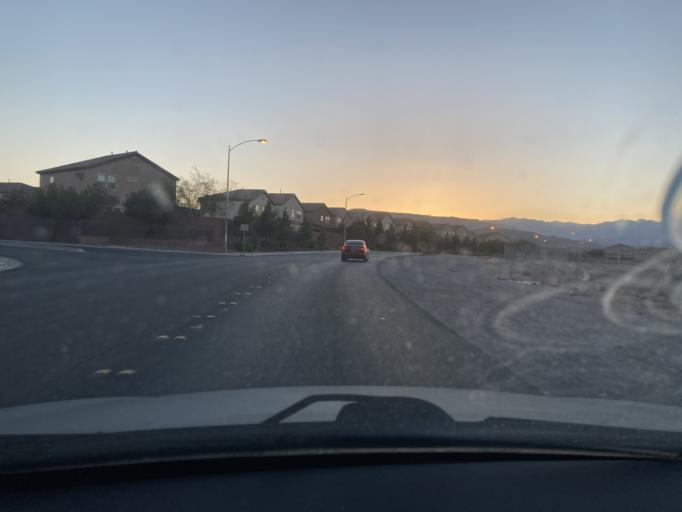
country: US
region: Nevada
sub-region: Clark County
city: Enterprise
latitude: 36.0611
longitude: -115.2842
